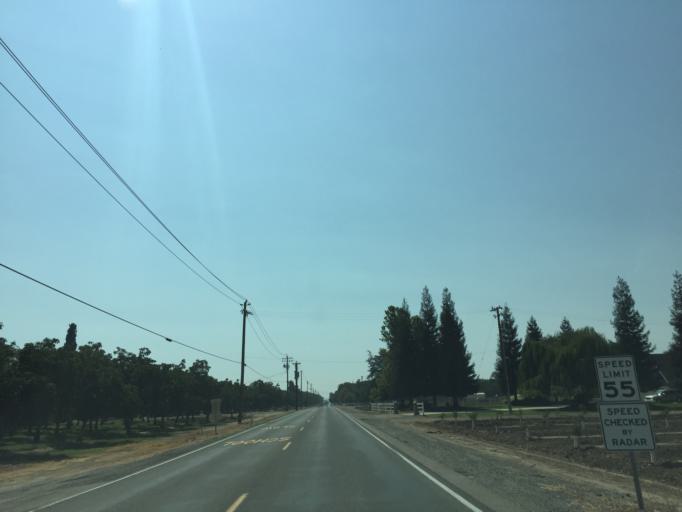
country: US
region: California
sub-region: Kings County
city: Lucerne
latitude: 36.4012
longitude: -119.6434
